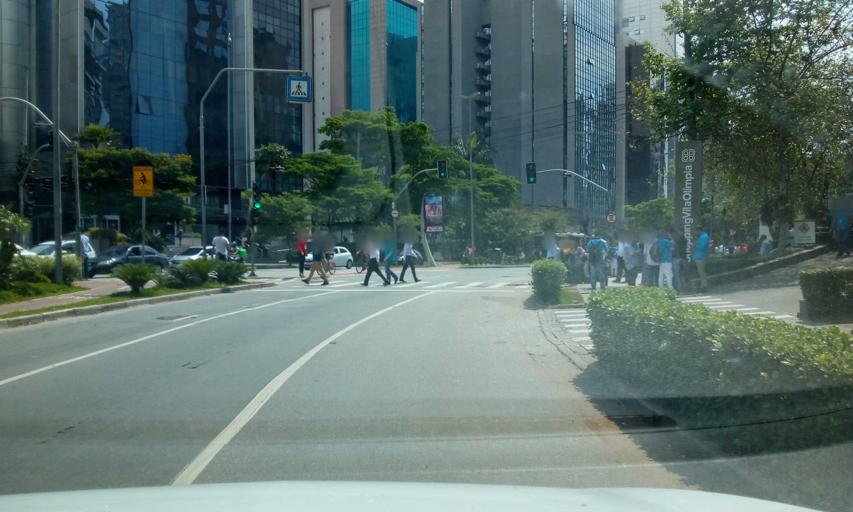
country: BR
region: Sao Paulo
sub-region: Sao Paulo
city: Sao Paulo
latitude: -23.5970
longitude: -46.6867
